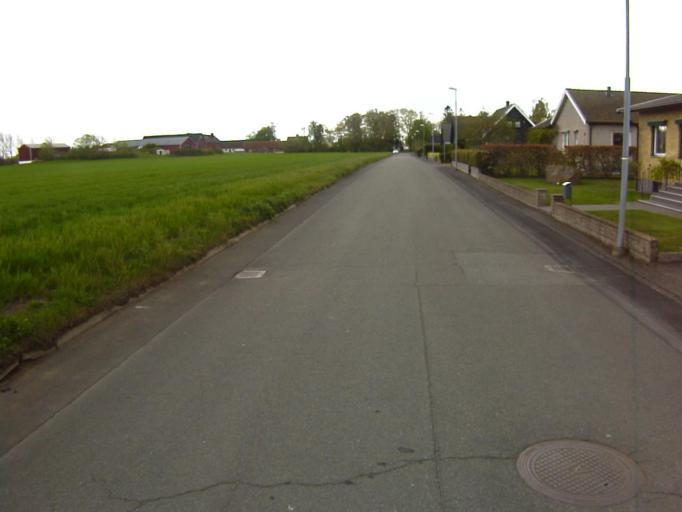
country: SE
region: Skane
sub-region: Kristianstads Kommun
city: Fjalkinge
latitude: 56.0165
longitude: 14.2345
